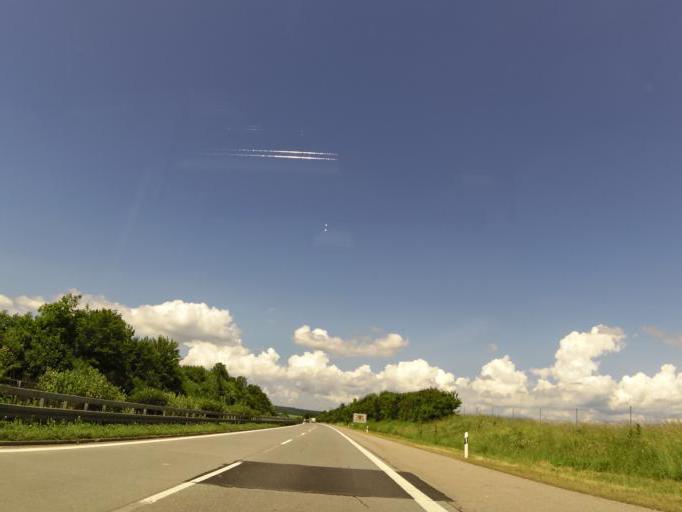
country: DE
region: Baden-Wuerttemberg
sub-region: Tuebingen Region
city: Langenau
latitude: 48.4761
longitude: 10.1087
